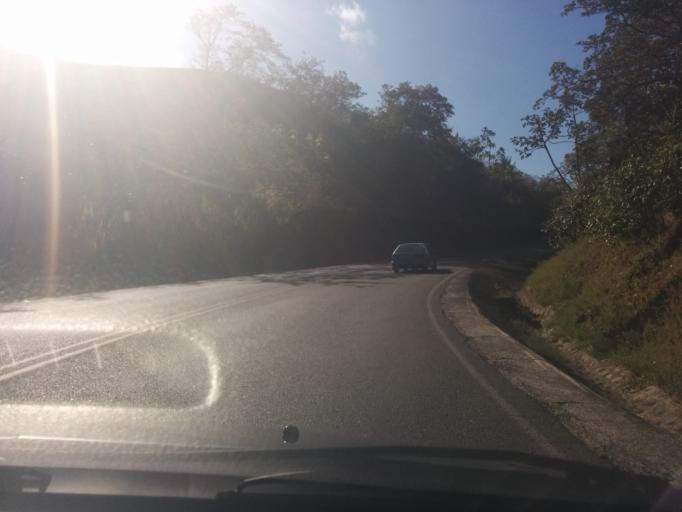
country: CR
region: Alajuela
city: San Rafael
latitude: 10.0373
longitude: -84.5073
